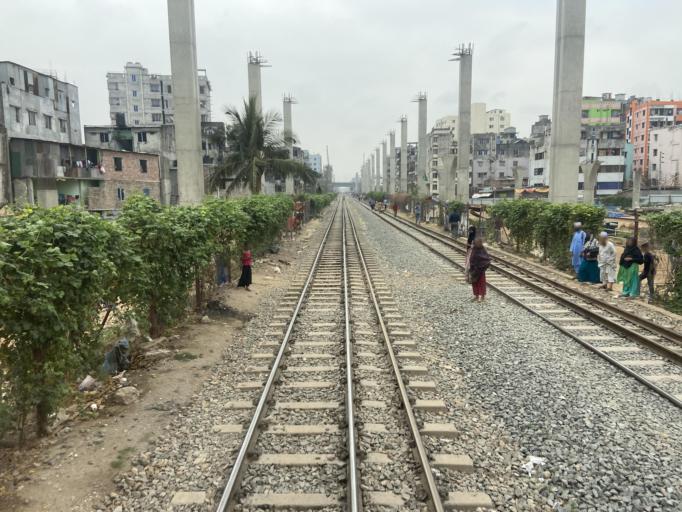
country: BD
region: Dhaka
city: Paltan
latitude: 23.7736
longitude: 90.3970
